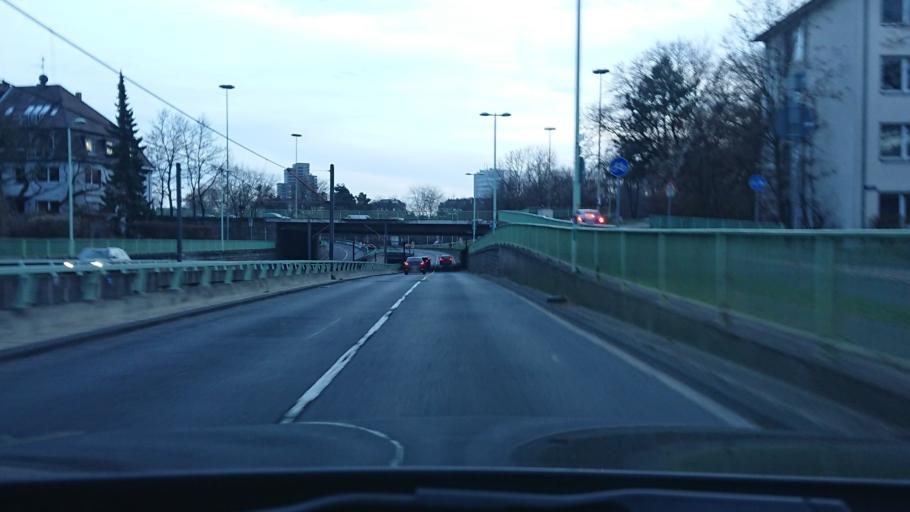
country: DE
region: North Rhine-Westphalia
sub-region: Regierungsbezirk Koln
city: Riehl
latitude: 50.9599
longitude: 6.9676
